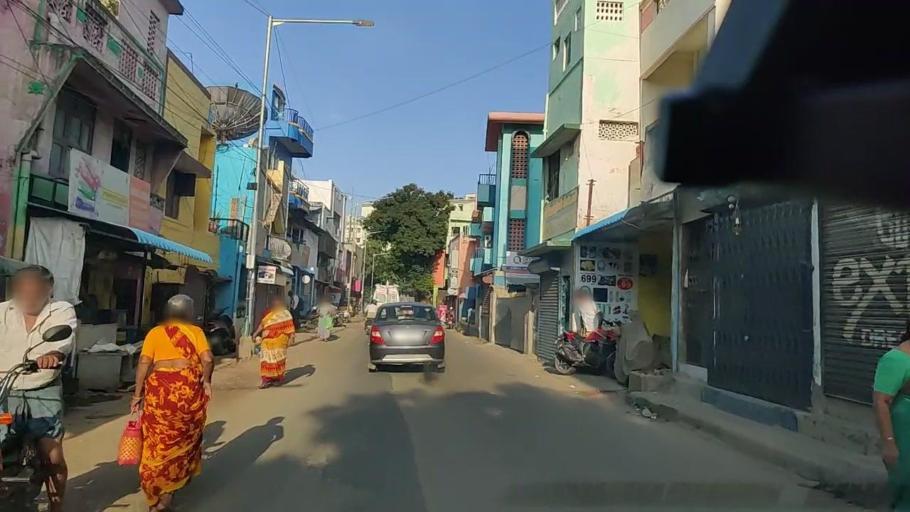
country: IN
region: Tamil Nadu
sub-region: Chennai
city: George Town
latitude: 13.1142
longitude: 80.2624
